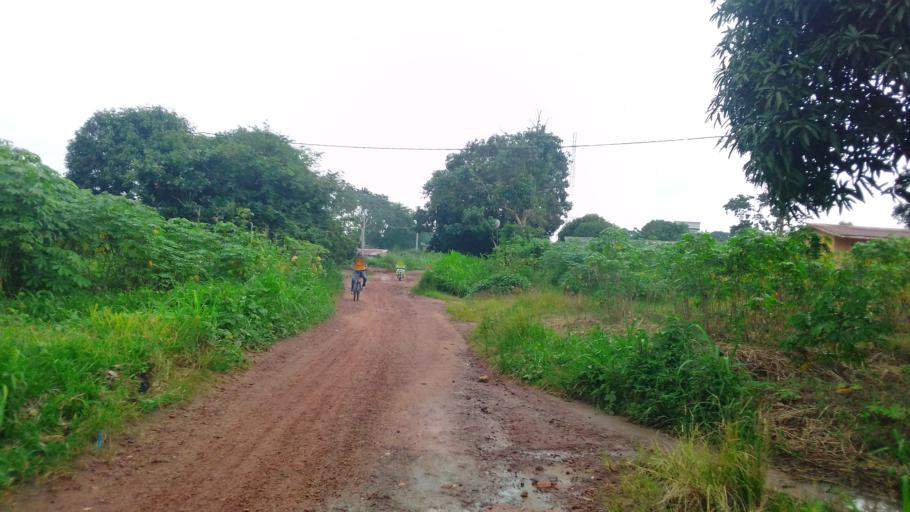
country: SL
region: Northern Province
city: Lunsar
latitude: 8.6865
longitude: -12.5254
